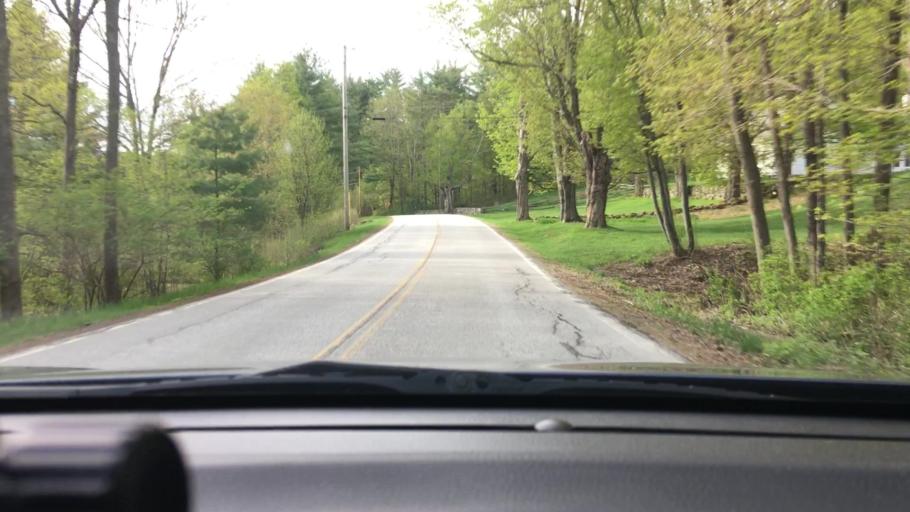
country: US
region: Vermont
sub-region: Bennington County
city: Manchester Center
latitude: 43.2206
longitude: -73.0738
